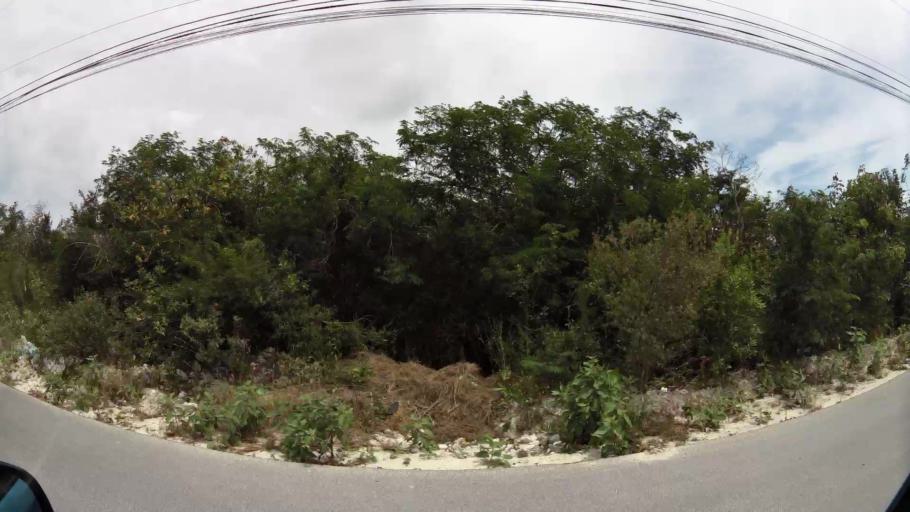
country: BS
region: Mayaguana
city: Abraham's Bay
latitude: 21.8068
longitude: -72.2961
